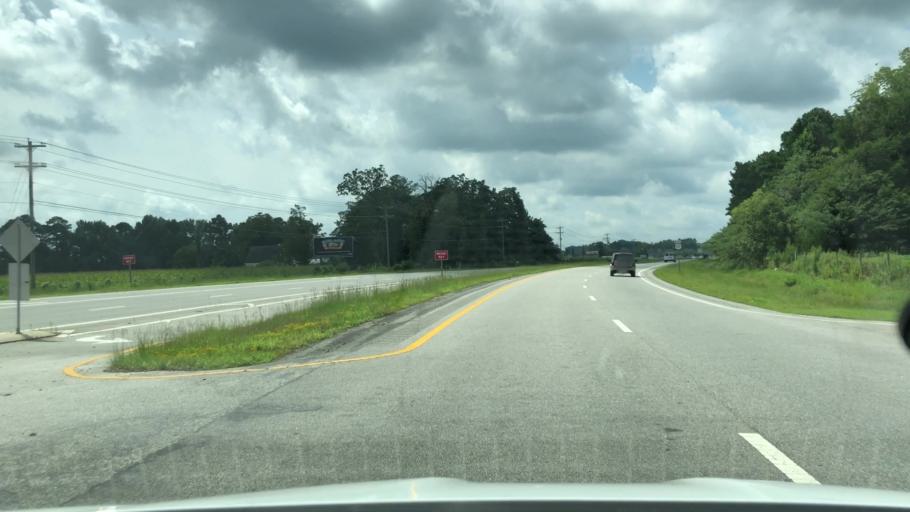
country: US
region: North Carolina
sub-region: Beaufort County
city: Washington
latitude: 35.4892
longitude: -77.1079
